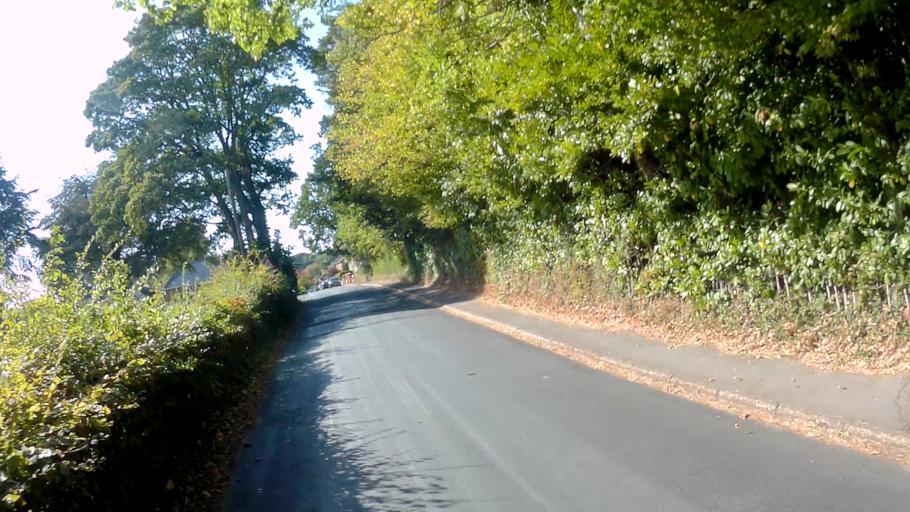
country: GB
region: England
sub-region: Surrey
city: Churt
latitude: 51.1732
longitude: -0.7934
